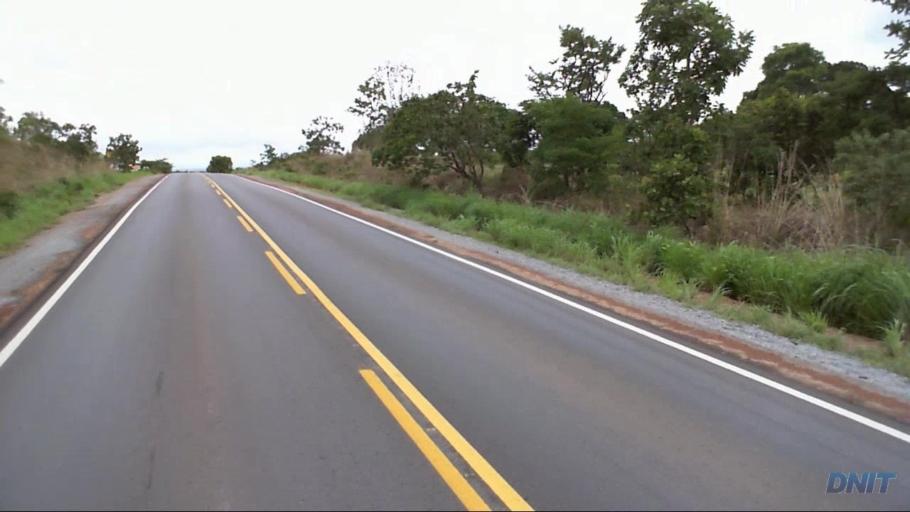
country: BR
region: Goias
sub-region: Padre Bernardo
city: Padre Bernardo
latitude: -15.4054
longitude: -48.2001
